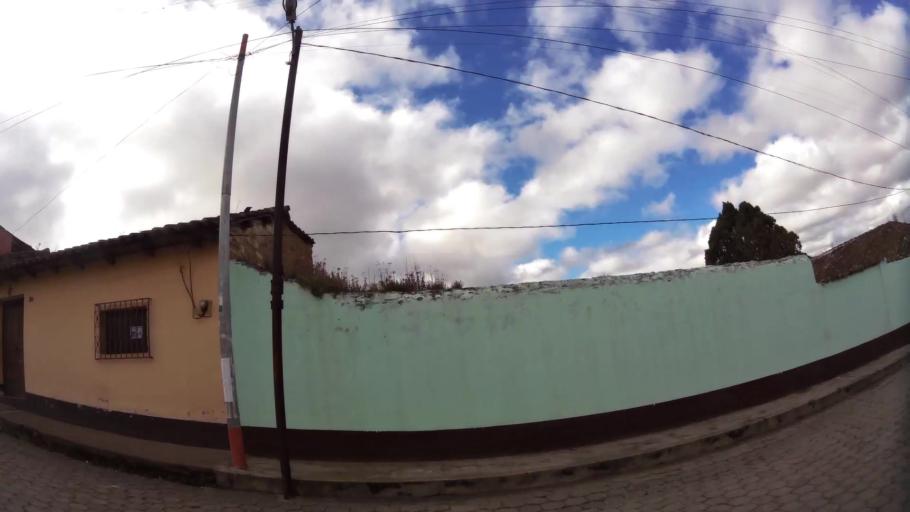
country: GT
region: Quetzaltenango
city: Salcaja
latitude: 14.8784
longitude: -91.4532
